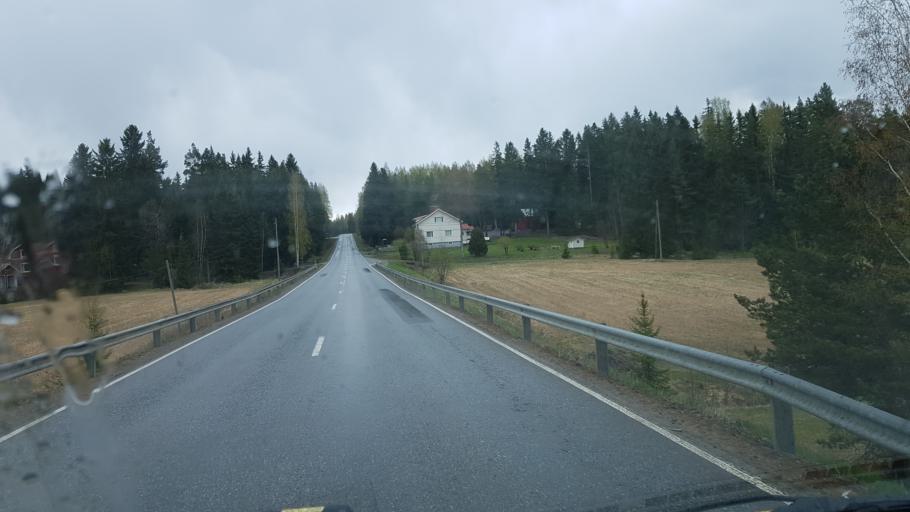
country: FI
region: Pirkanmaa
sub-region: Tampere
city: Pirkkala
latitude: 61.3928
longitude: 23.6226
